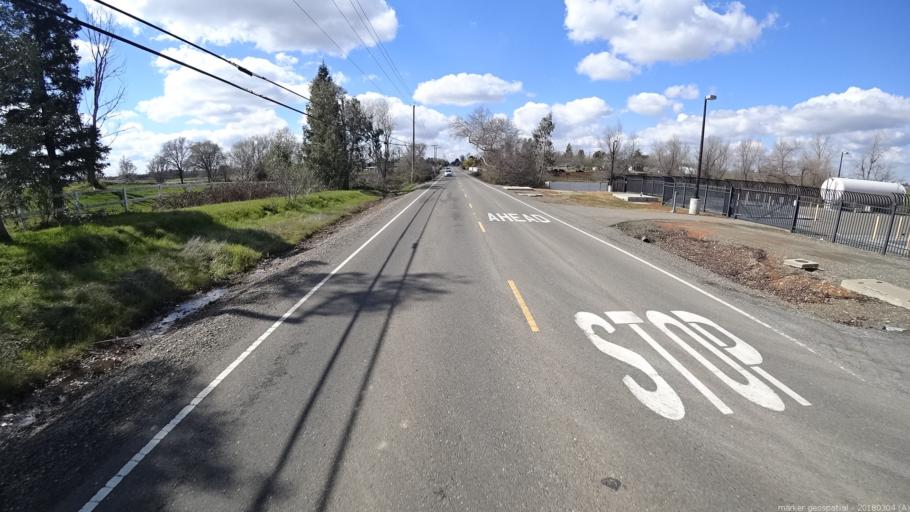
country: US
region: California
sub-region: Sacramento County
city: Vineyard
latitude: 38.4817
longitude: -121.3138
